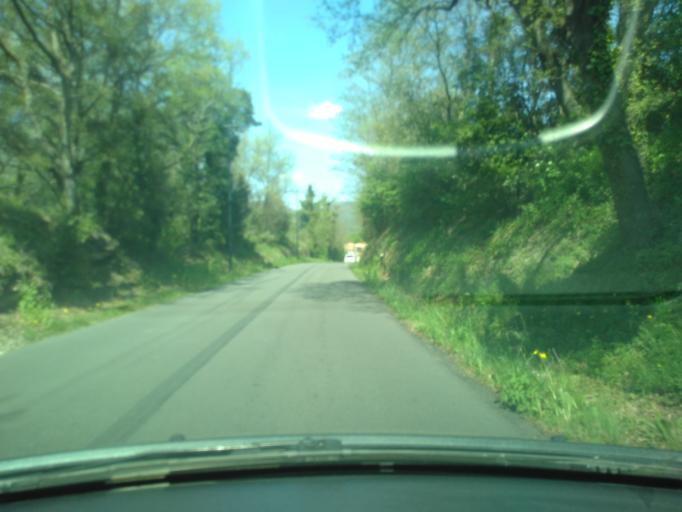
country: FR
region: Rhone-Alpes
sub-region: Departement de la Drome
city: Taulignan
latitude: 44.4399
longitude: 4.9786
